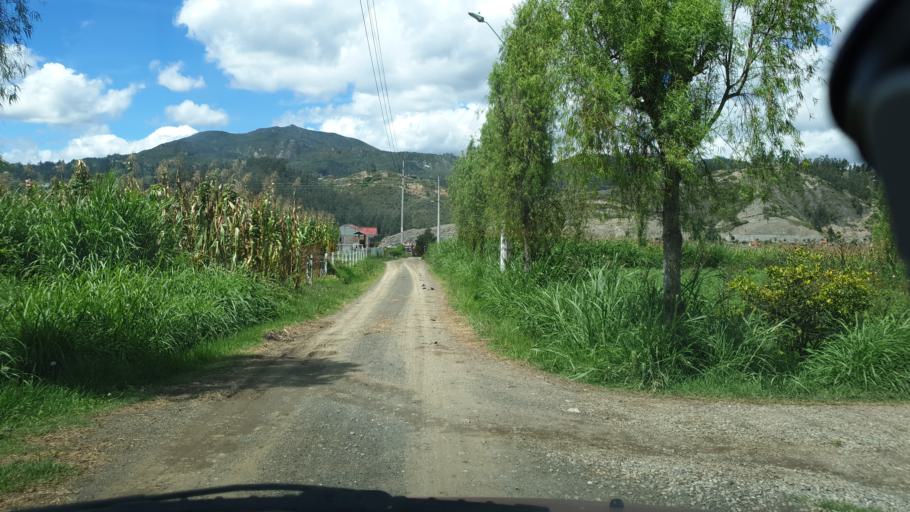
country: EC
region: Azuay
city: Cuenca
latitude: -2.8739
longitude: -78.9497
